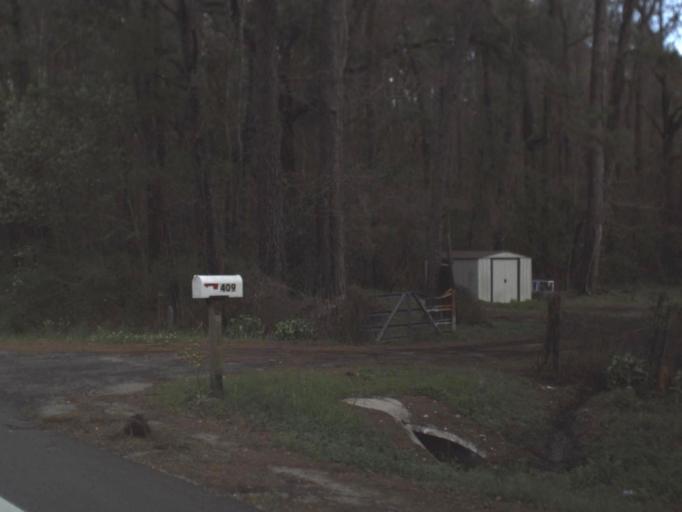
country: US
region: Florida
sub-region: Leon County
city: Woodville
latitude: 30.2864
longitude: -84.3527
